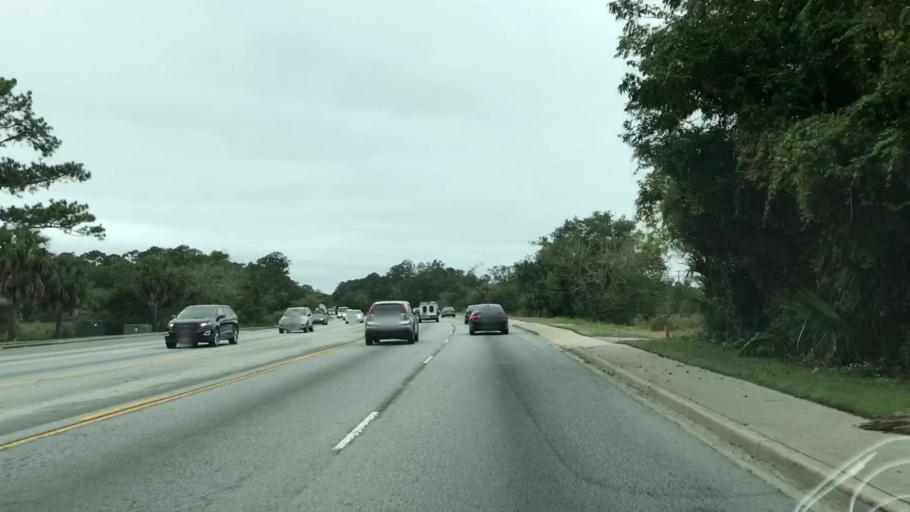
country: US
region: South Carolina
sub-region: Beaufort County
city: Hilton Head Island
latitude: 32.2179
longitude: -80.7601
